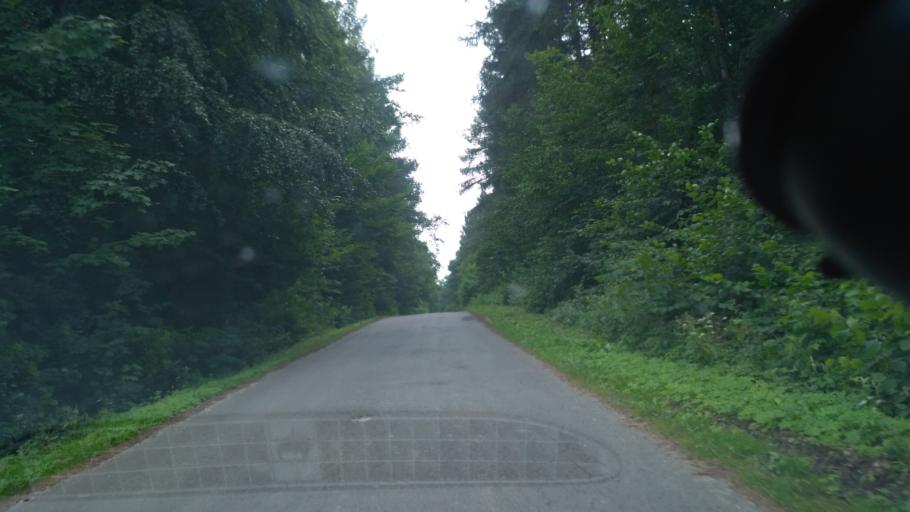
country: PL
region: Subcarpathian Voivodeship
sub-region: Powiat przeworski
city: Lopuszka Wielka
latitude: 49.9094
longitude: 22.3982
